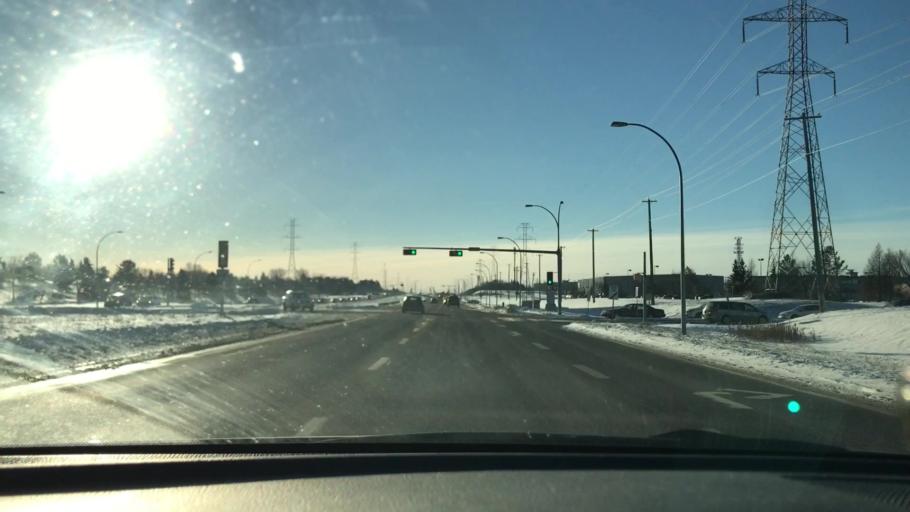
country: CA
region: Alberta
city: Edmonton
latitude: 53.4573
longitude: -113.4669
